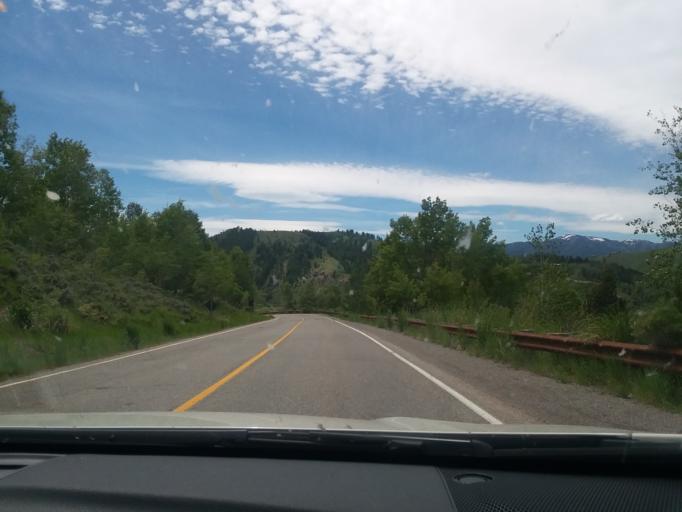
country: US
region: Wyoming
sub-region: Teton County
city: Jackson
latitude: 43.4937
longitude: -110.7842
